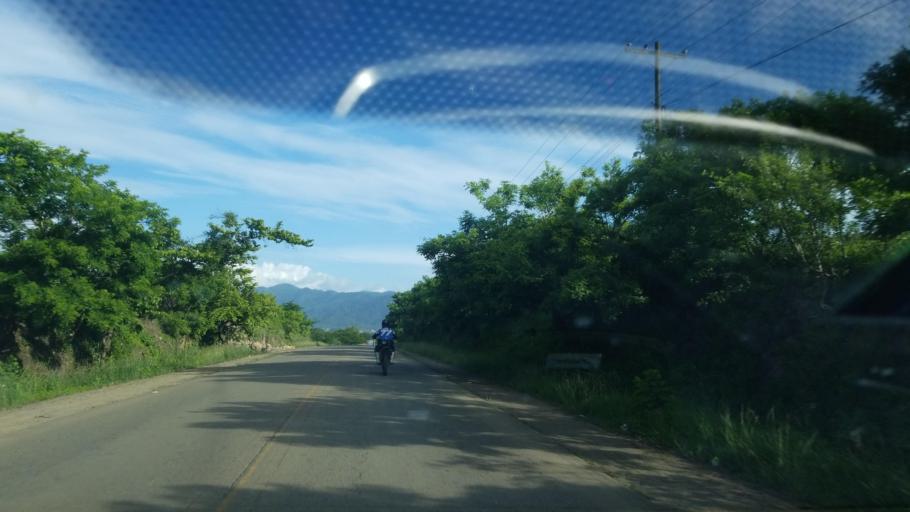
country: HN
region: El Paraiso
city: Cuyali
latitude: 13.9059
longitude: -86.5561
